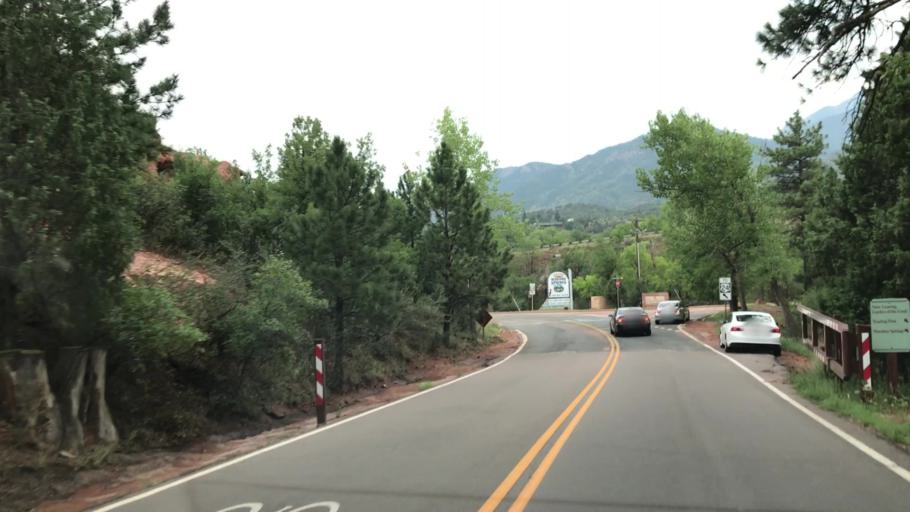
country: US
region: Colorado
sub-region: El Paso County
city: Manitou Springs
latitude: 38.8608
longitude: -104.8978
